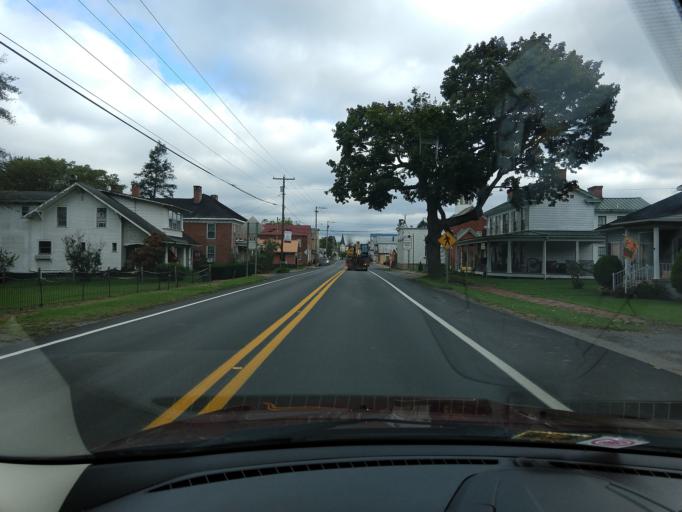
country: US
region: West Virginia
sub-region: Randolph County
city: Elkins
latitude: 38.8400
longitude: -79.8759
